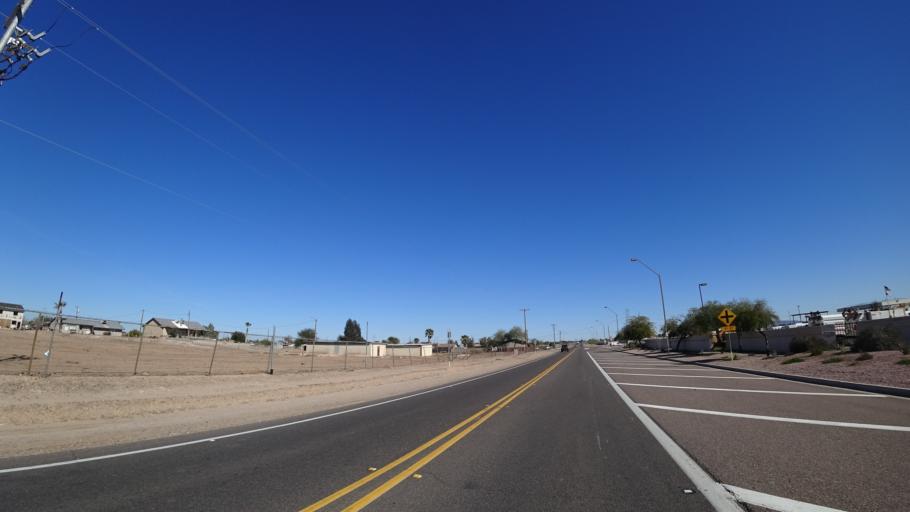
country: US
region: Arizona
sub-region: Maricopa County
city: Avondale
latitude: 33.4208
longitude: -112.3470
